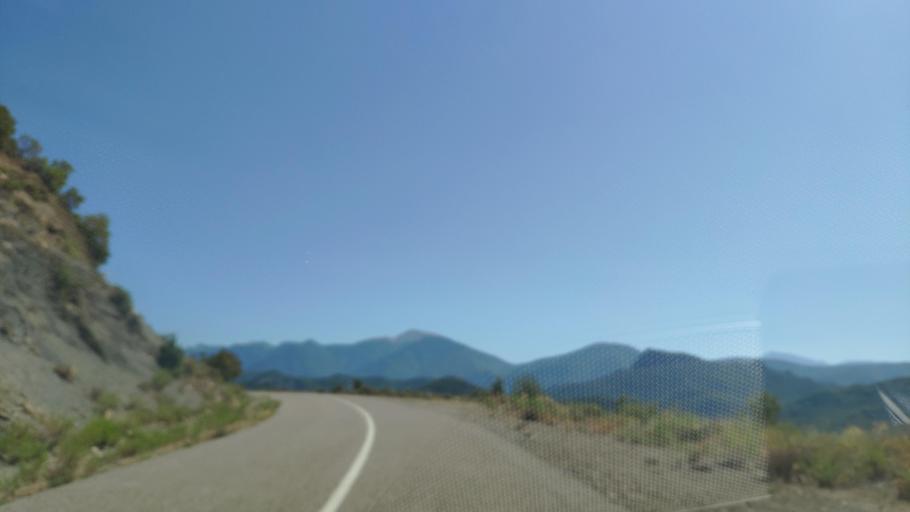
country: GR
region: Central Greece
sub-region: Nomos Evrytanias
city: Kerasochori
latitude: 38.9850
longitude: 21.5010
